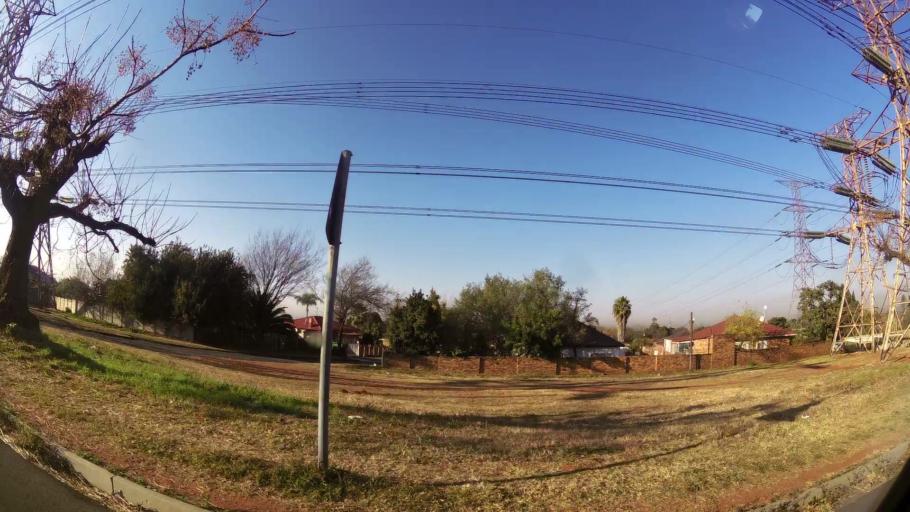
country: ZA
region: Gauteng
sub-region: Ekurhuleni Metropolitan Municipality
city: Germiston
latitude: -26.1922
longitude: 28.1458
